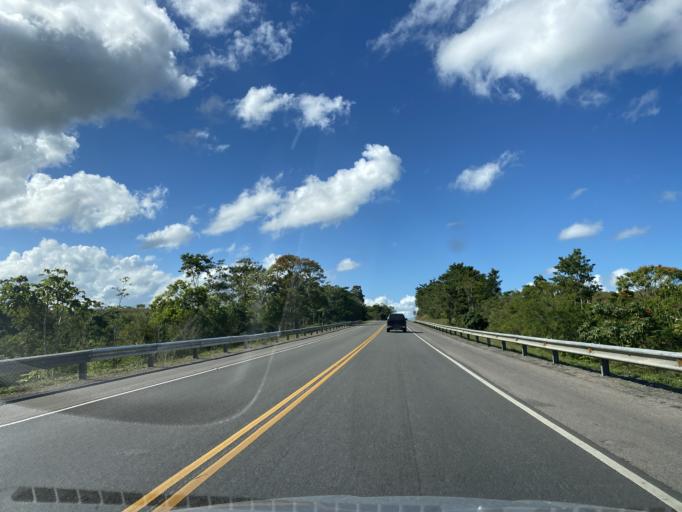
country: DO
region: Monte Plata
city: Gonzalo
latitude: 18.9665
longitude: -69.7709
